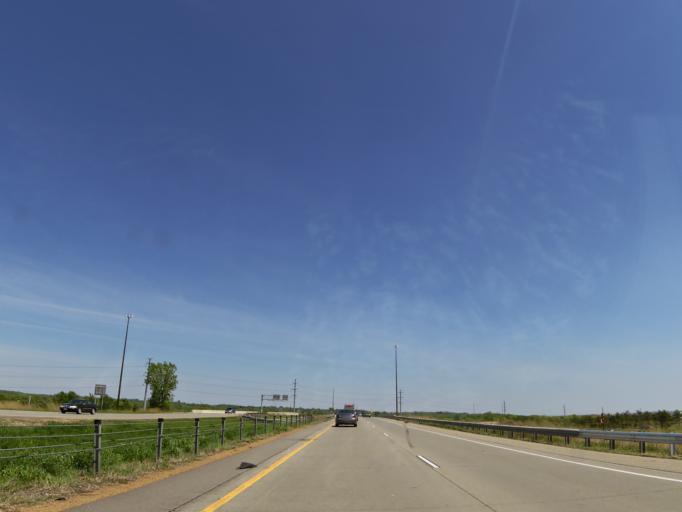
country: US
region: Minnesota
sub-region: Scott County
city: Prior Lake
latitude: 44.7853
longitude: -93.4152
